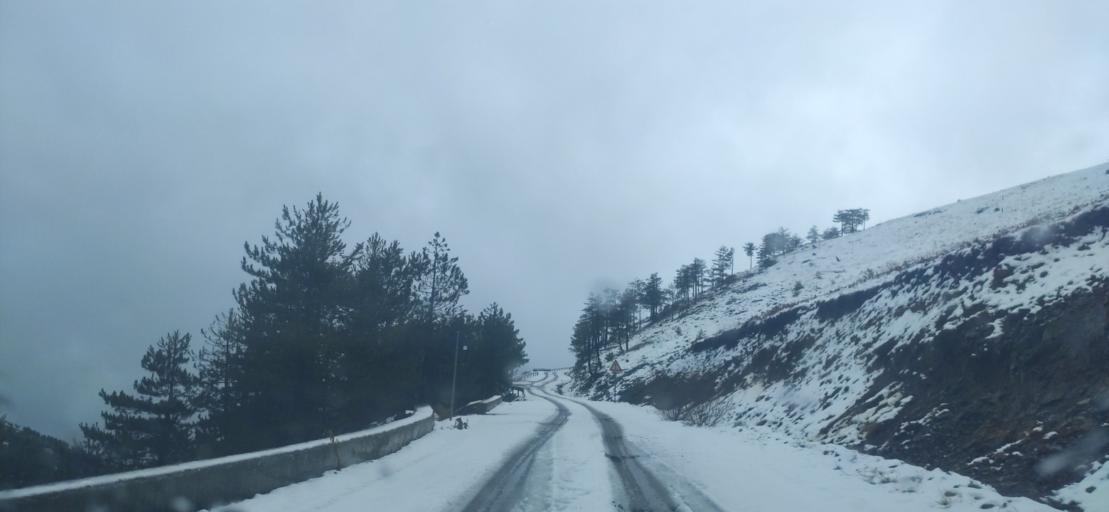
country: AL
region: Shkoder
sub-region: Rrethi i Pukes
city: Iballe
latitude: 42.1493
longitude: 20.0494
